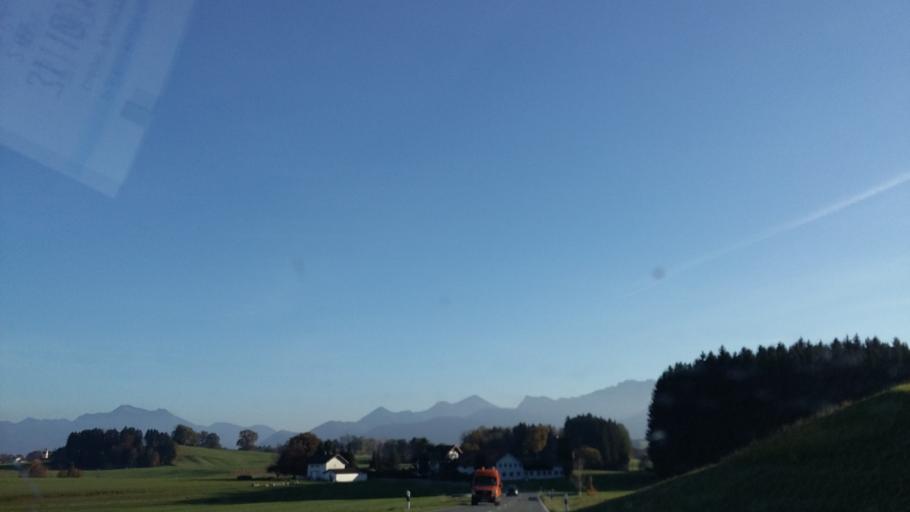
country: DE
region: Bavaria
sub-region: Upper Bavaria
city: Rimsting
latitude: 47.8610
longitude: 12.3166
